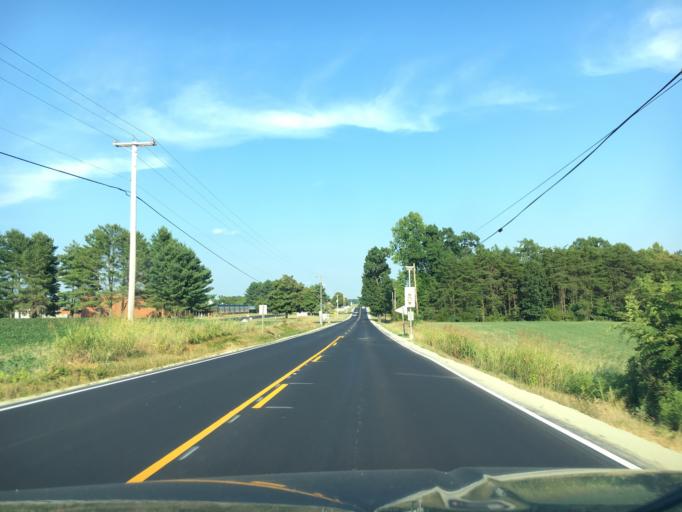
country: US
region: Virginia
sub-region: Franklin County
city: Union Hall
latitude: 36.9872
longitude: -79.7515
